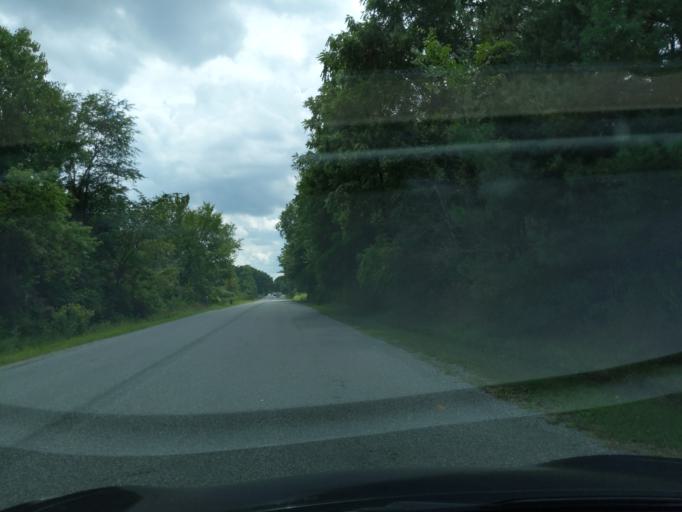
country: US
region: Michigan
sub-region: Eaton County
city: Dimondale
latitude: 42.6437
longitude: -84.5825
